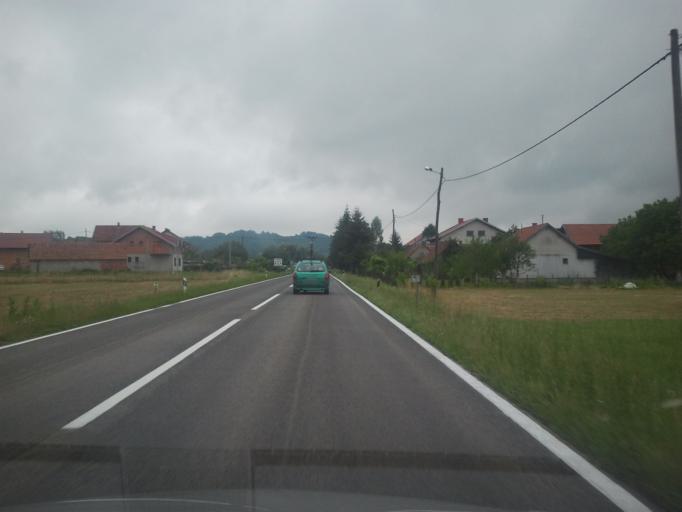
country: HR
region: Karlovacka
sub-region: Grad Karlovac
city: Karlovac
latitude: 45.3991
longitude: 15.6135
